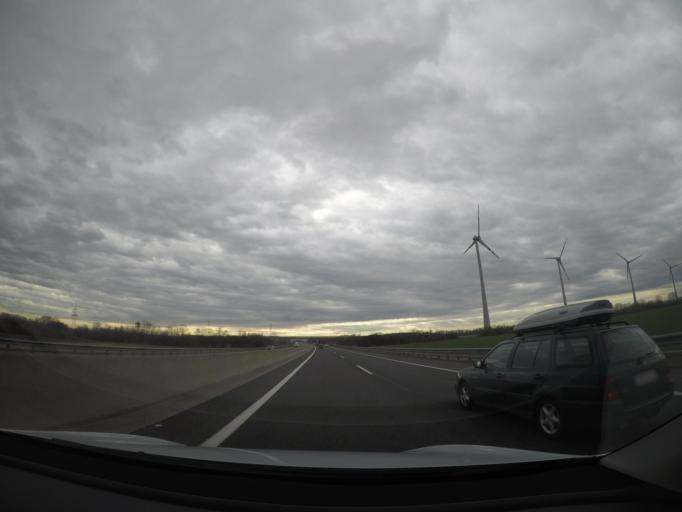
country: AT
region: Lower Austria
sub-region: Politischer Bezirk Baden
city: Ebreichsdorf
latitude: 47.9405
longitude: 16.3754
